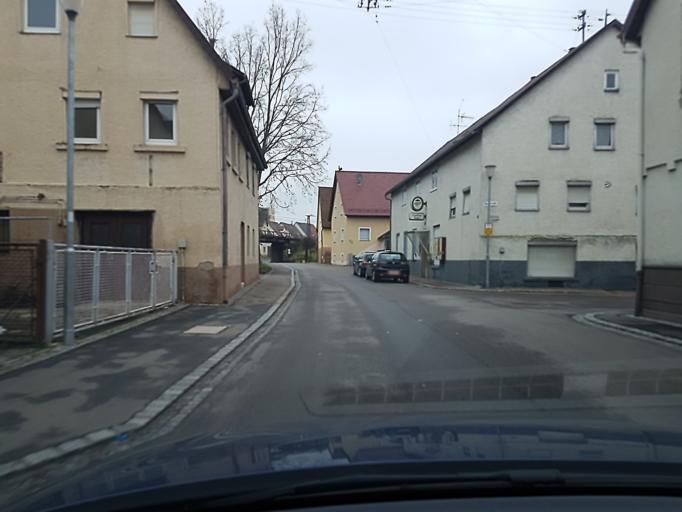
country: DE
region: Baden-Wuerttemberg
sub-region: Regierungsbezirk Stuttgart
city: Walheim
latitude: 49.0123
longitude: 9.1536
